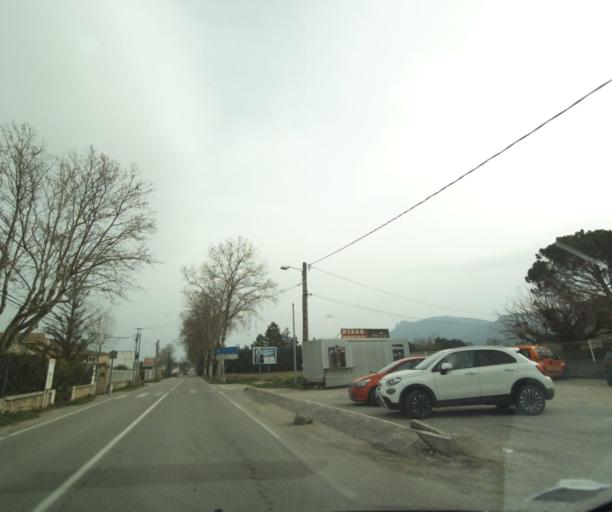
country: FR
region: Provence-Alpes-Cote d'Azur
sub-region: Departement des Bouches-du-Rhone
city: Trets
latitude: 43.4501
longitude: 5.6913
